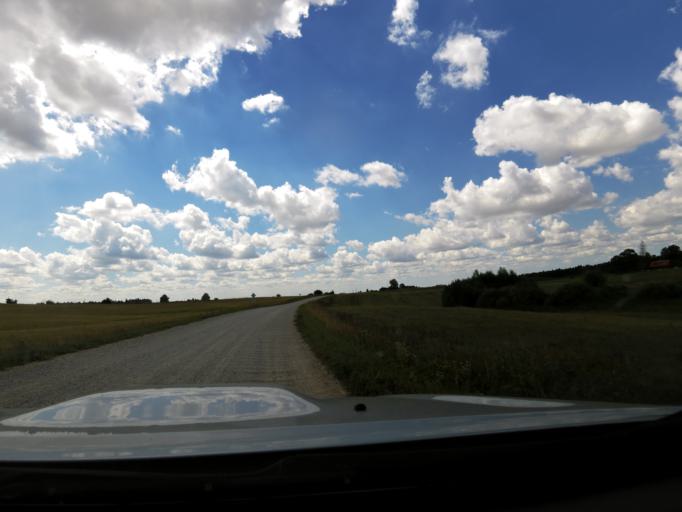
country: LT
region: Vilnius County
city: Elektrenai
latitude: 54.9094
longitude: 24.6476
